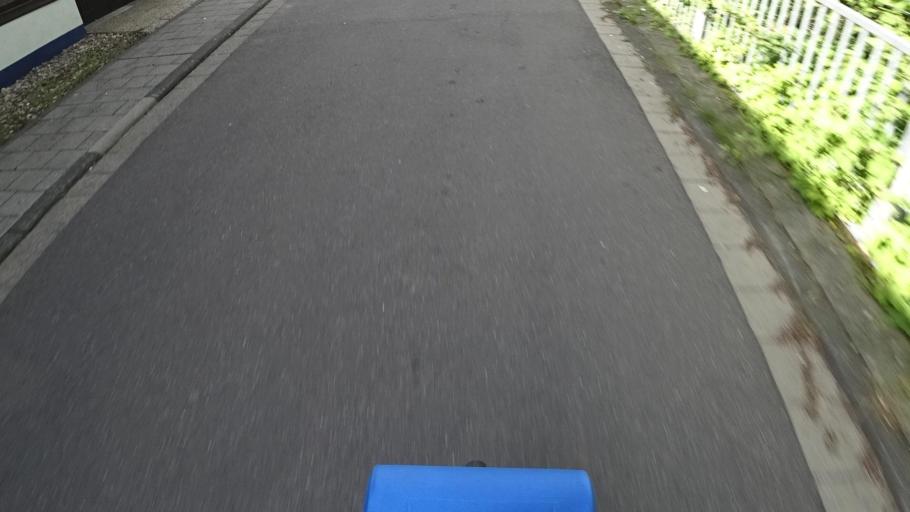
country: DE
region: Rheinland-Pfalz
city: Vettelschoss
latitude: 50.6140
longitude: 7.3418
